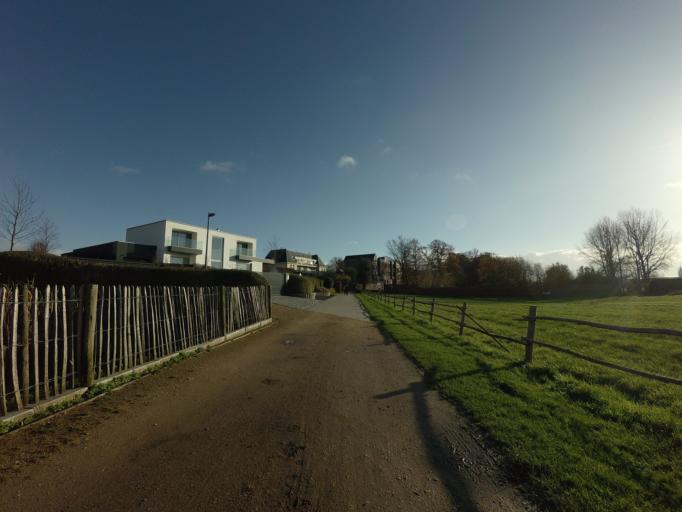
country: BE
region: Flanders
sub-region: Provincie Antwerpen
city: Niel
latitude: 51.1097
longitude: 4.3199
